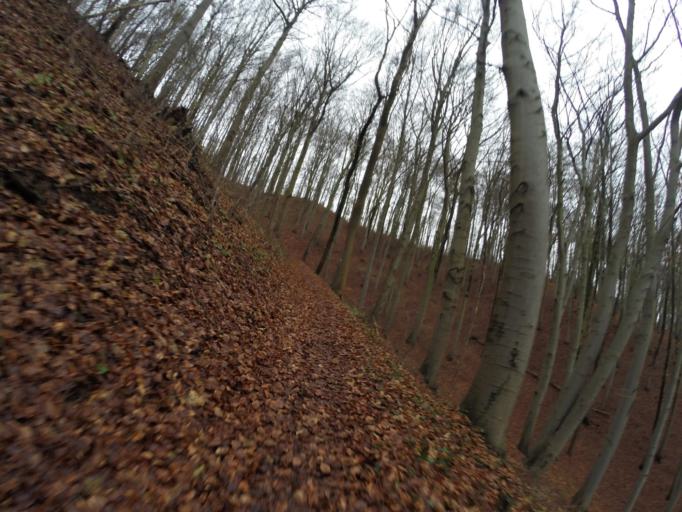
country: DE
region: Thuringia
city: Jena
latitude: 50.9175
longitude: 11.6220
